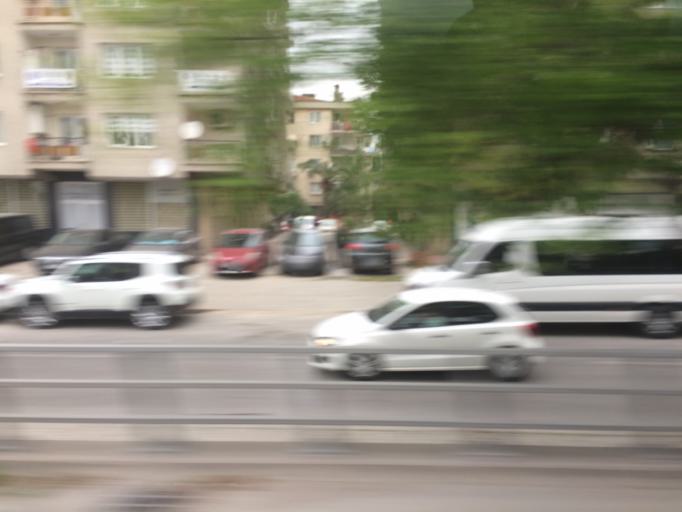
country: TR
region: Izmir
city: Bornova
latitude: 38.4552
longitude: 27.1989
